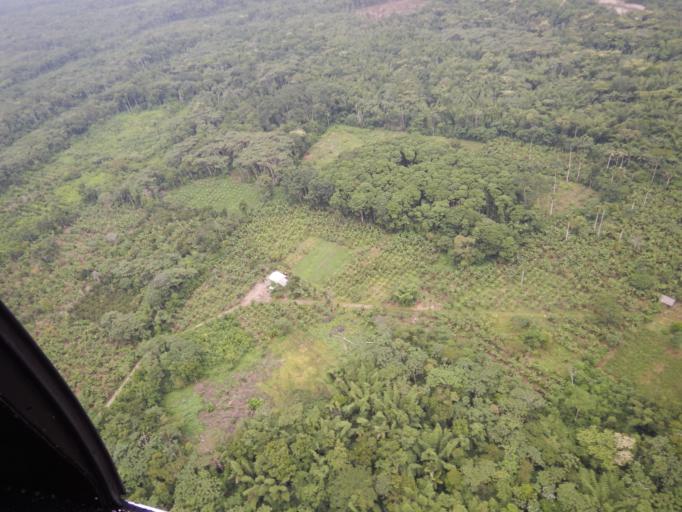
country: BO
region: Cochabamba
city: Chimore
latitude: -17.2456
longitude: -64.6387
